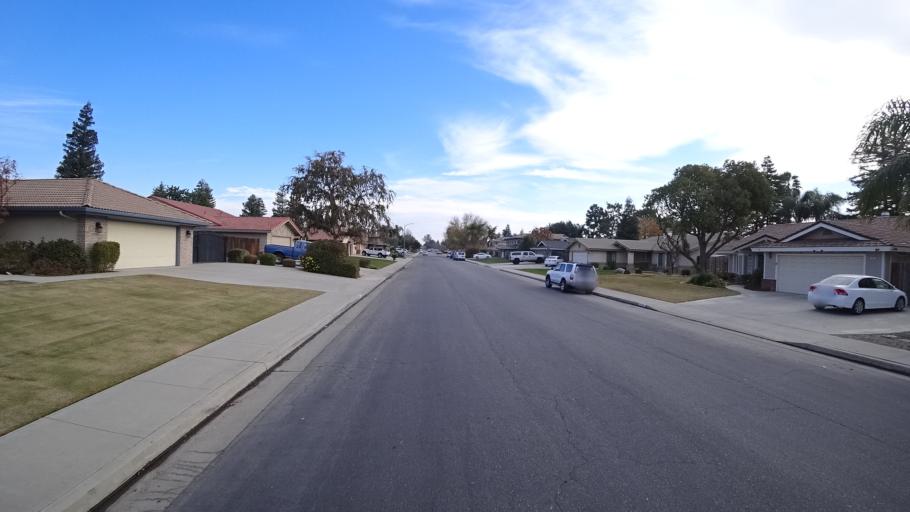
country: US
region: California
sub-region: Kern County
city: Greenacres
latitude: 35.4048
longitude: -119.0822
